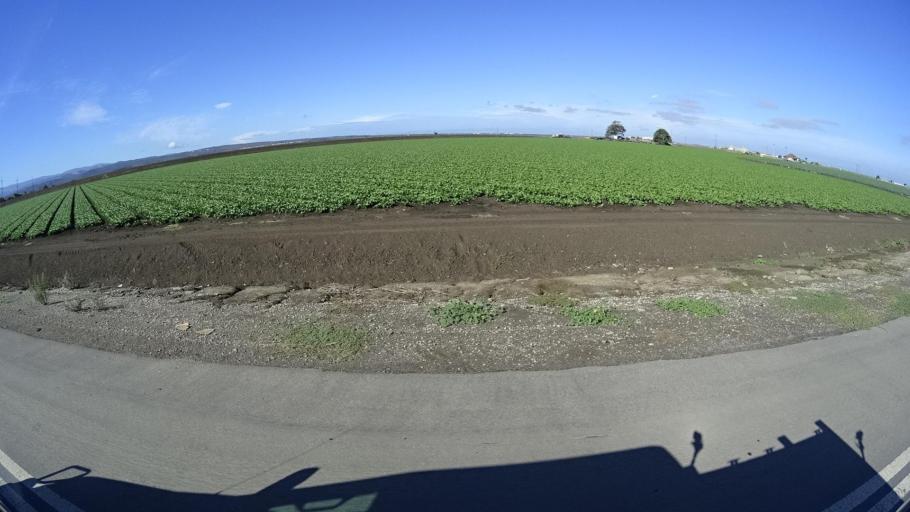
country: US
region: California
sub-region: Monterey County
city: Boronda
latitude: 36.6804
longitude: -121.6749
